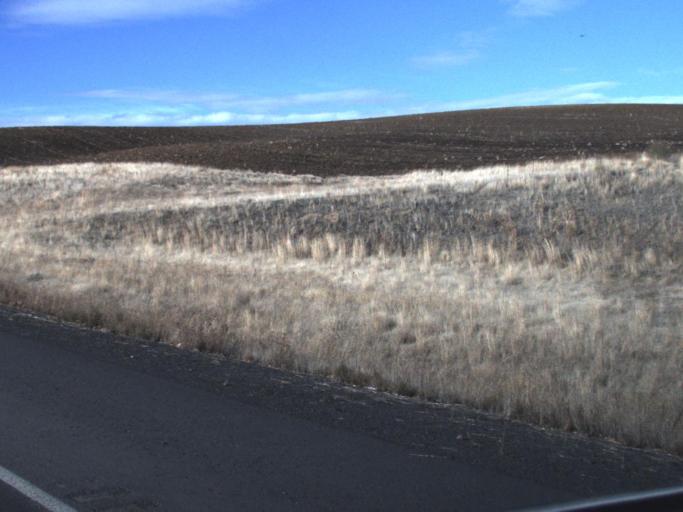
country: US
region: Idaho
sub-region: Latah County
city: Moscow
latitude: 46.7389
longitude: -117.0593
